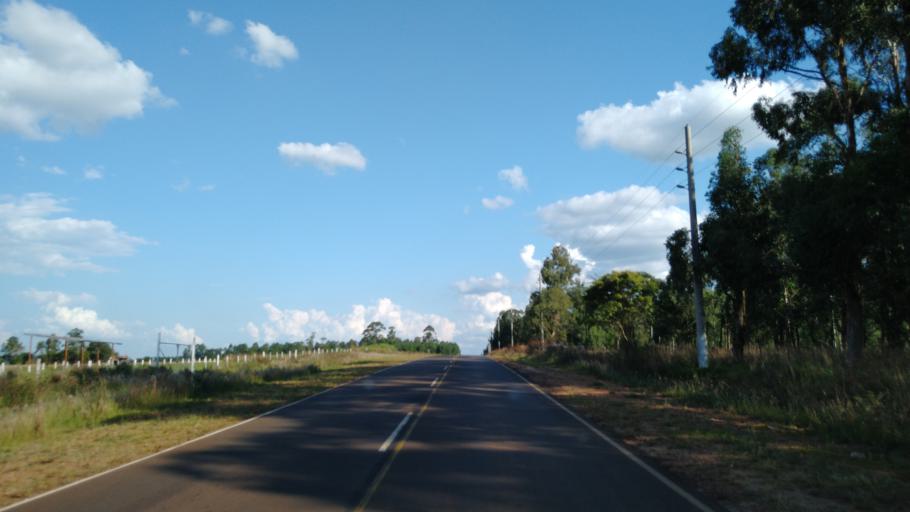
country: PY
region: Itapua
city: San Juan del Parana
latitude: -27.3765
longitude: -55.9921
